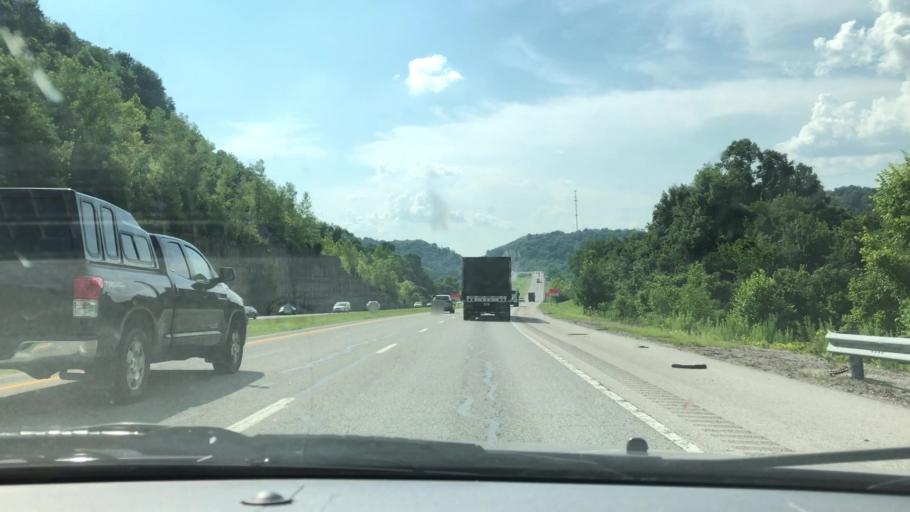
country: US
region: Tennessee
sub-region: Williamson County
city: Thompson's Station
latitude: 35.8164
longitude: -86.8097
